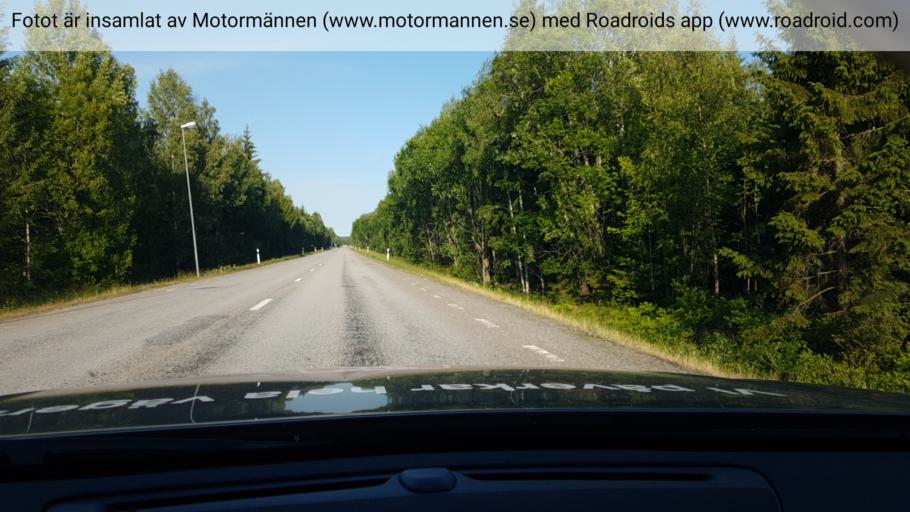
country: SE
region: Uppsala
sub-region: Osthammars Kommun
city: Gimo
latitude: 60.1651
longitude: 18.1571
